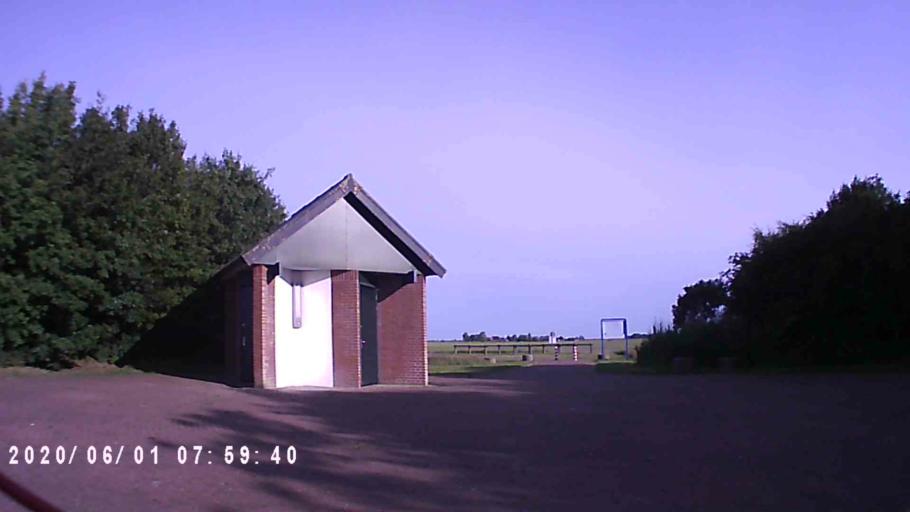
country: NL
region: Friesland
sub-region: Gemeente Dantumadiel
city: Rinsumageast
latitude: 53.2827
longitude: 5.9371
